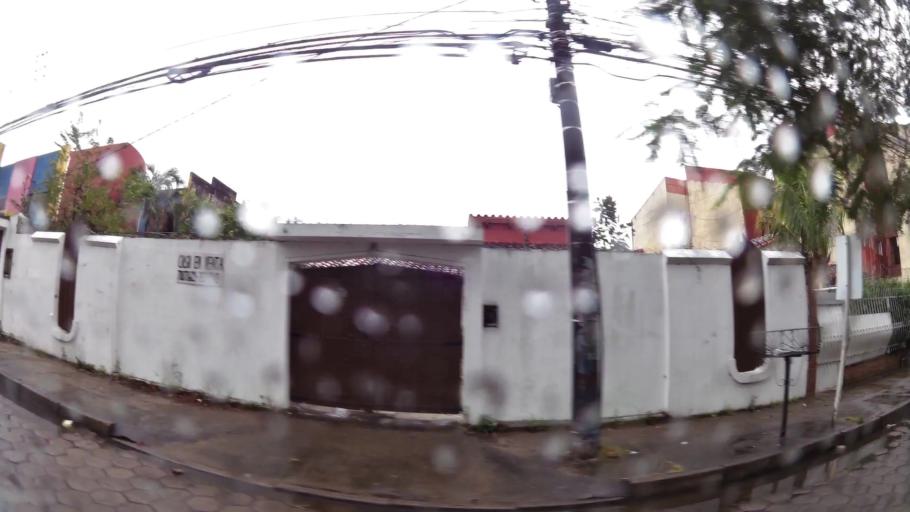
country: BO
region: Santa Cruz
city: Santa Cruz de la Sierra
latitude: -17.7786
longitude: -63.1672
